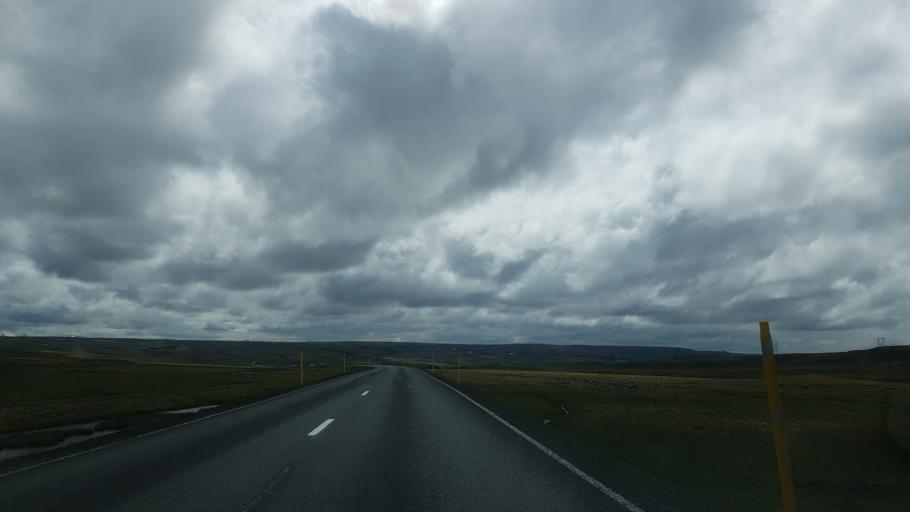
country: IS
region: West
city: Borgarnes
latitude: 64.9601
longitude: -21.0605
